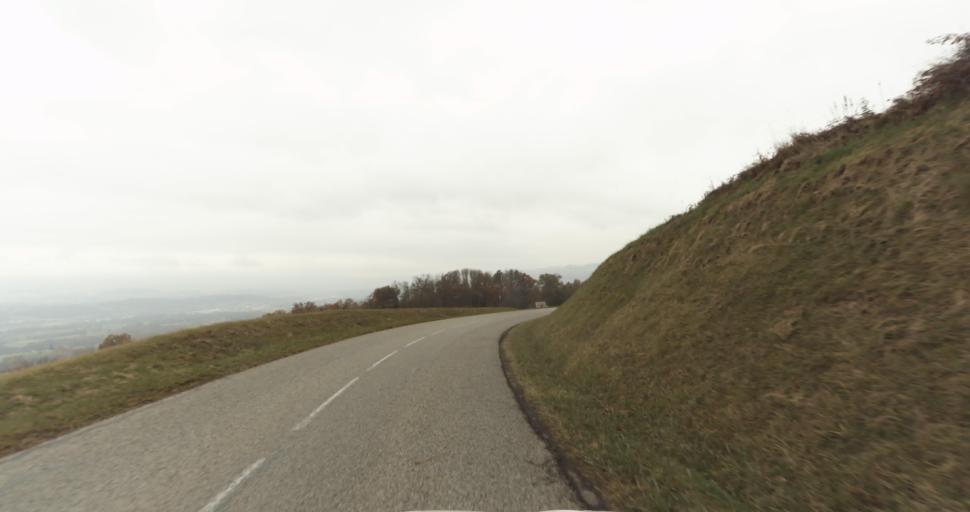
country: FR
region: Rhone-Alpes
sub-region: Departement de la Haute-Savoie
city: Saint-Felix
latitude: 45.8037
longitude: 5.9953
